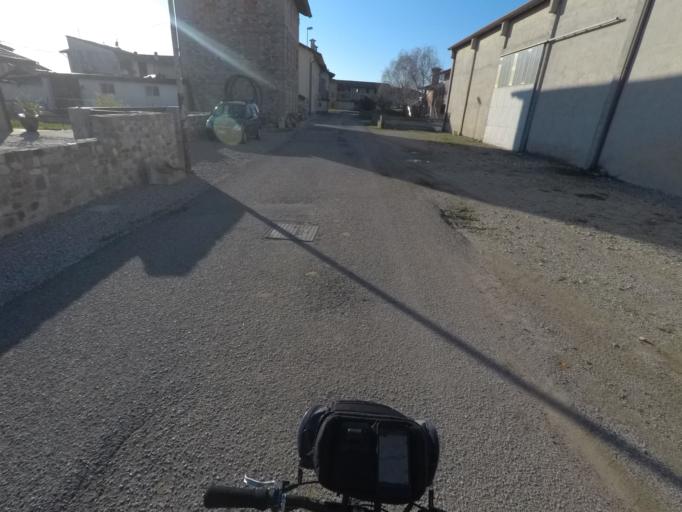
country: IT
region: Friuli Venezia Giulia
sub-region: Provincia di Udine
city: Povoletto
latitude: 46.1143
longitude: 13.2875
